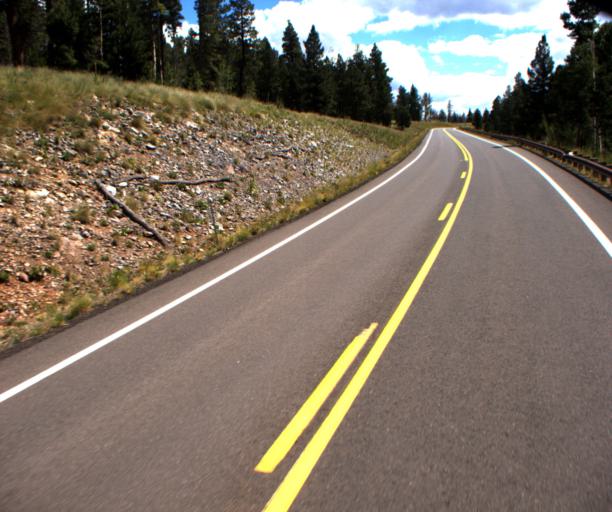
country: US
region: Arizona
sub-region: Apache County
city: Eagar
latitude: 33.9291
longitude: -109.4756
